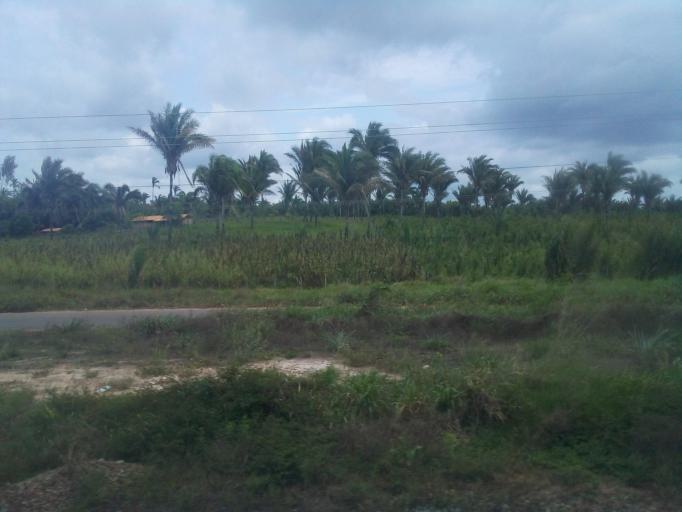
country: BR
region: Maranhao
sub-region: Santa Ines
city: Santa Ines
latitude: -3.7034
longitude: -45.9310
